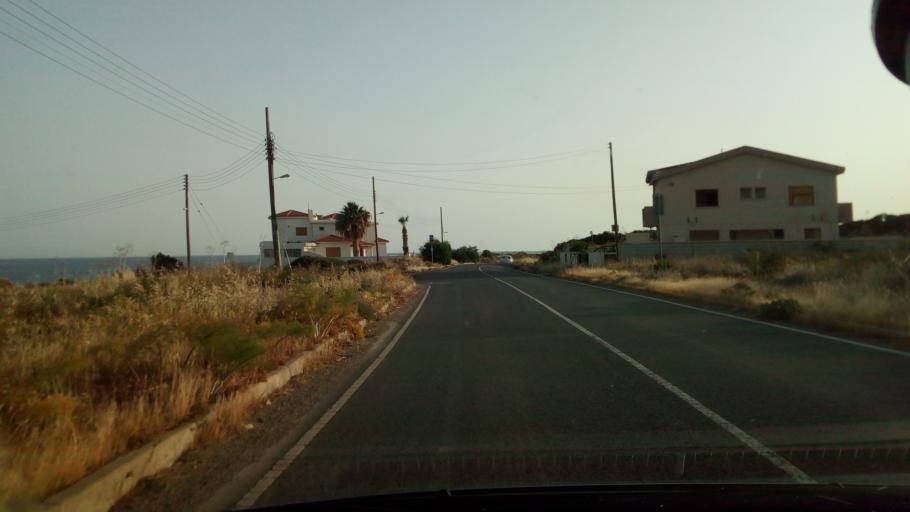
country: CY
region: Larnaka
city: Kofinou
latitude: 34.7686
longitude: 33.4417
